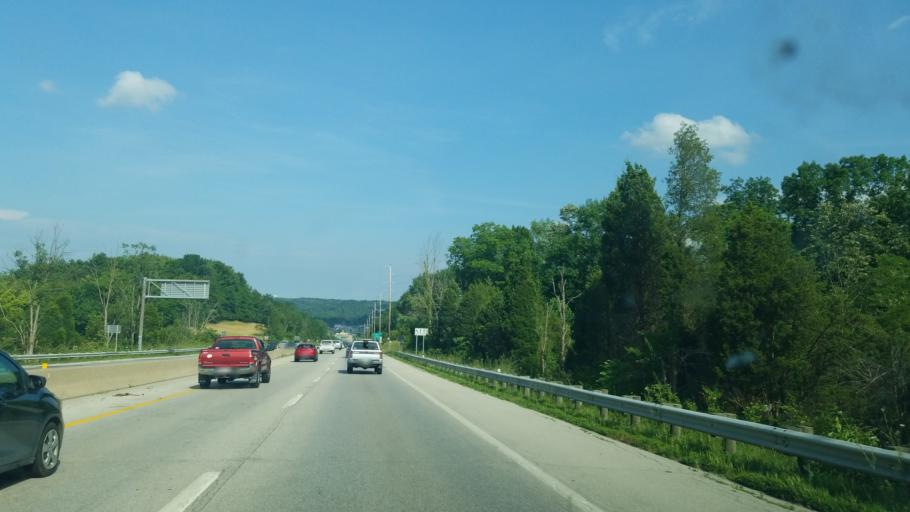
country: US
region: Ohio
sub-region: Clermont County
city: Batavia
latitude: 39.0876
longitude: -84.2053
